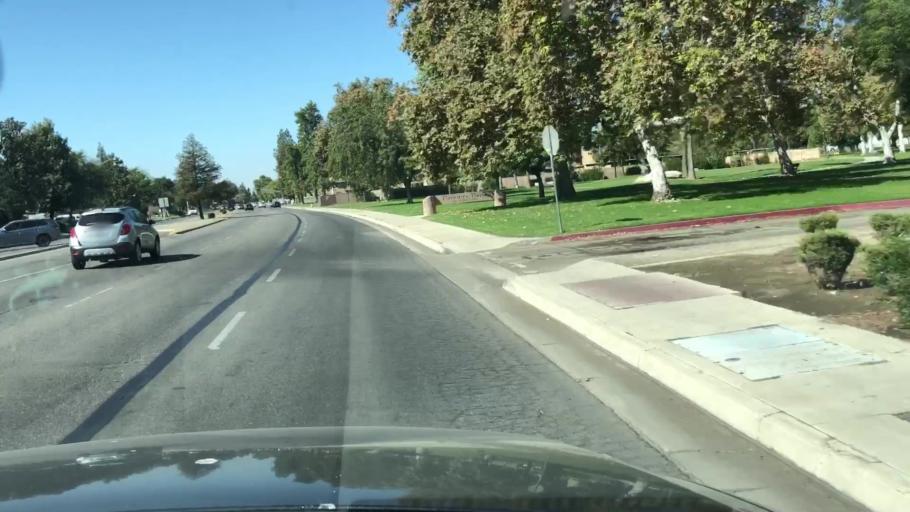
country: US
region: California
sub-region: Kern County
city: Bakersfield
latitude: 35.3393
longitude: -119.0578
